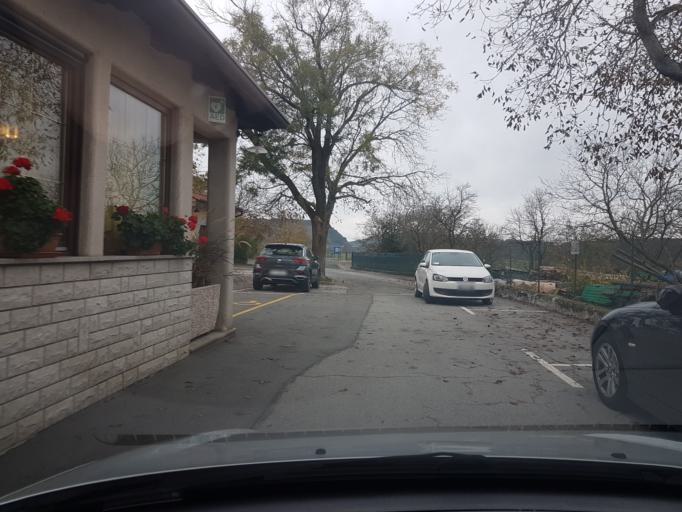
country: SI
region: Divaca
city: Divaca
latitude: 45.7317
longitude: 14.0118
